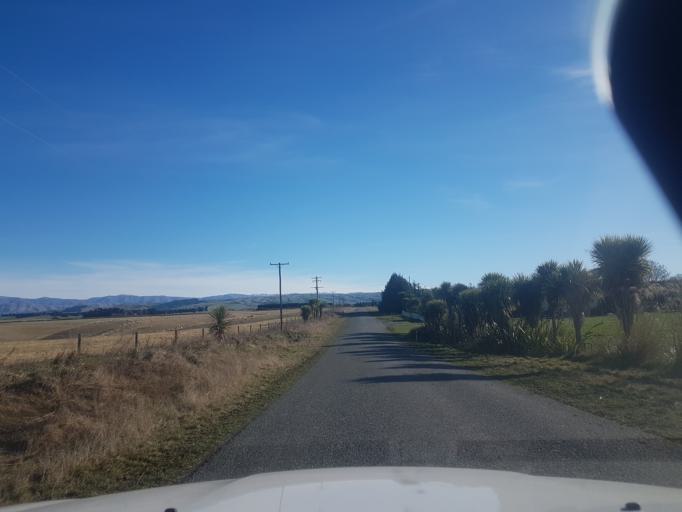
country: NZ
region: Canterbury
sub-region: Timaru District
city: Pleasant Point
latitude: -44.2546
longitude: 171.0332
